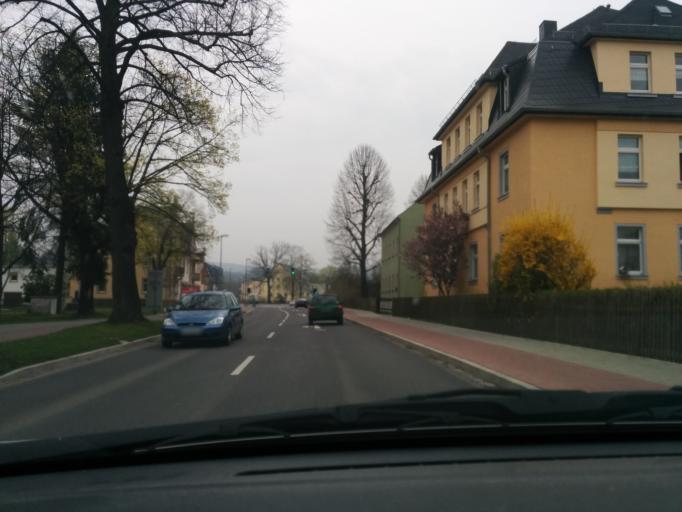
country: DE
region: Saxony
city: Floha
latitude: 50.8522
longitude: 13.0749
